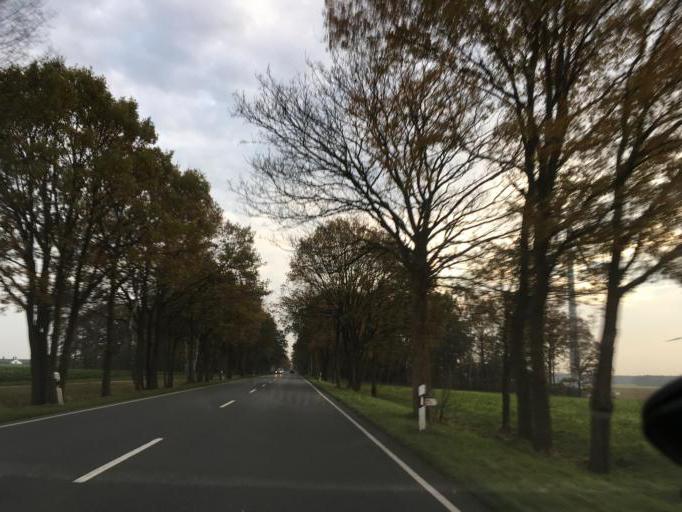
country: DE
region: Lower Saxony
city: Bergen
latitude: 52.7871
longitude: 9.9735
